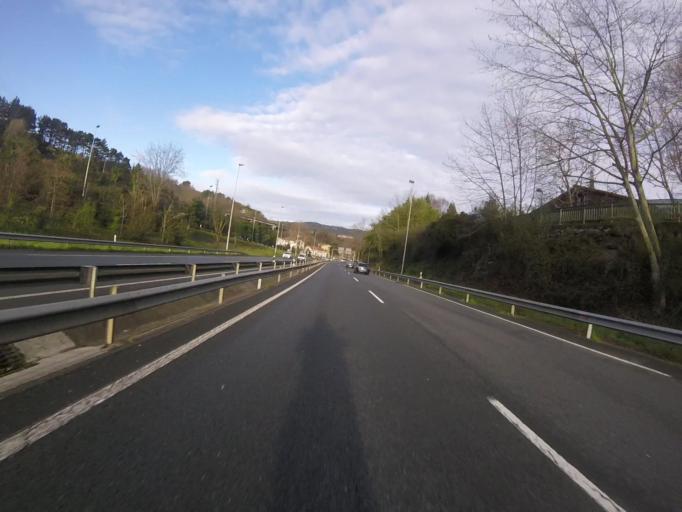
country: ES
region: Basque Country
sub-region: Provincia de Guipuzcoa
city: San Sebastian
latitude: 43.2970
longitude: -1.9973
